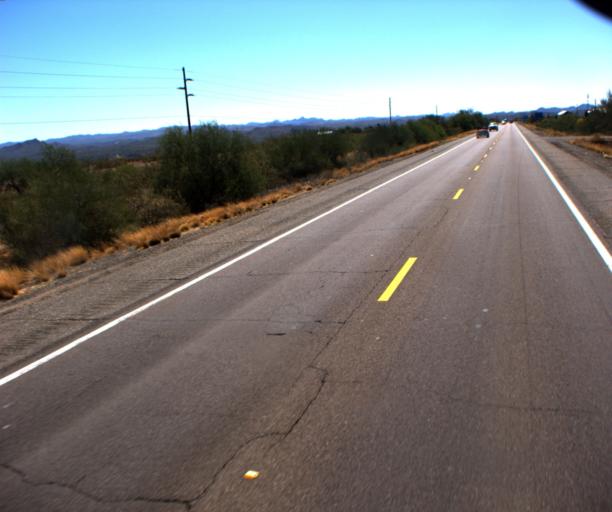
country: US
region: Arizona
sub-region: Maricopa County
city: Wickenburg
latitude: 34.0065
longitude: -112.7786
